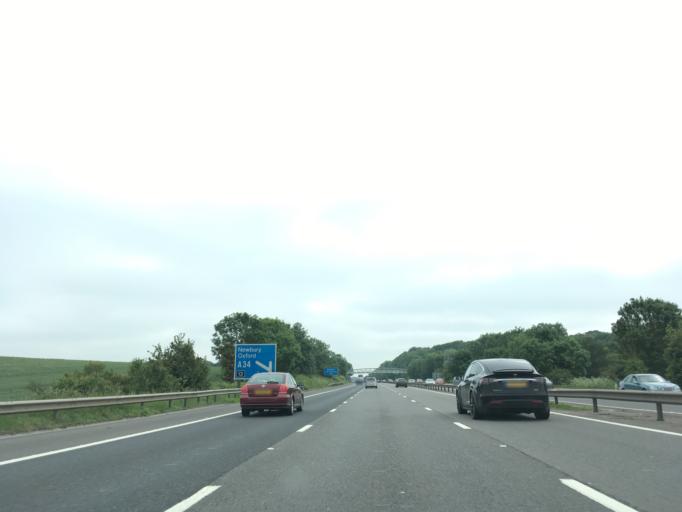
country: GB
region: England
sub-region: West Berkshire
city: Winterbourne
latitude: 51.4539
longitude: -1.3324
